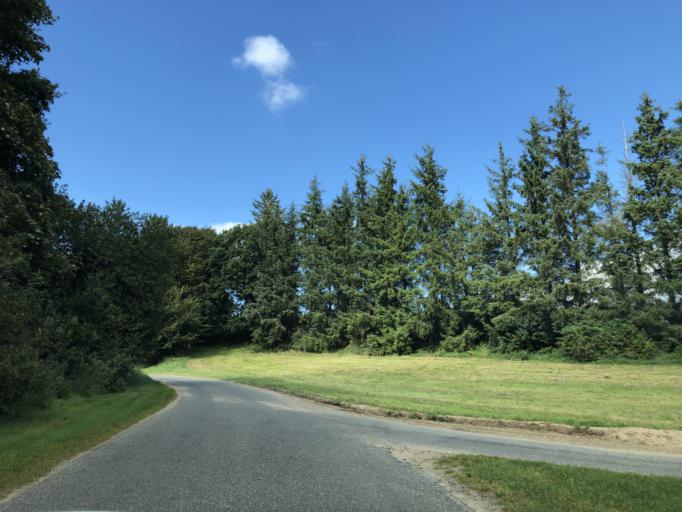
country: DK
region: Central Jutland
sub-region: Viborg Kommune
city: Viborg
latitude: 56.5669
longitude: 9.3221
